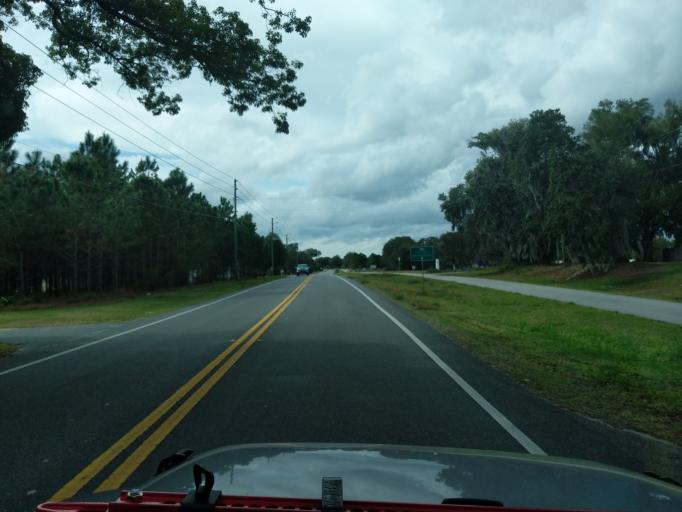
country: US
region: Florida
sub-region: Lake County
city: Clermont
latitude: 28.5755
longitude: -81.7907
